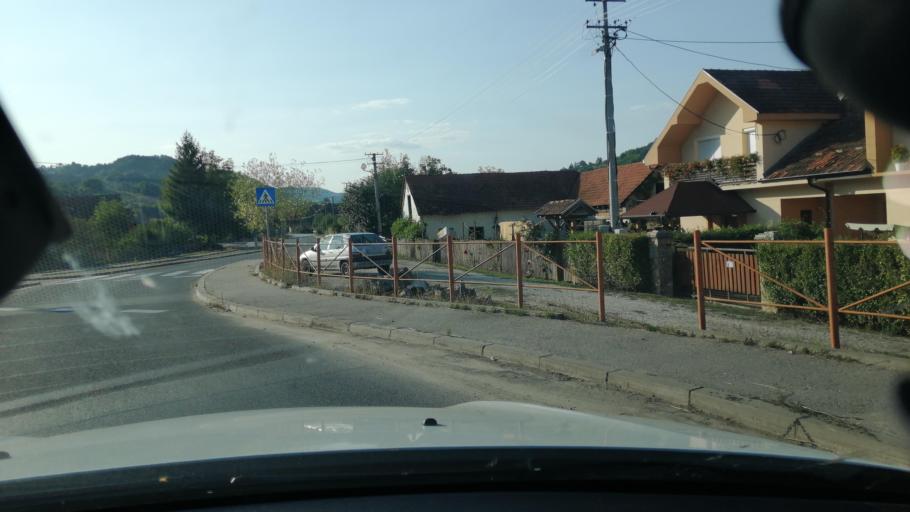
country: RS
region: Central Serbia
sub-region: Moravicki Okrug
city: Lucani
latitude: 43.7541
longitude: 20.2559
